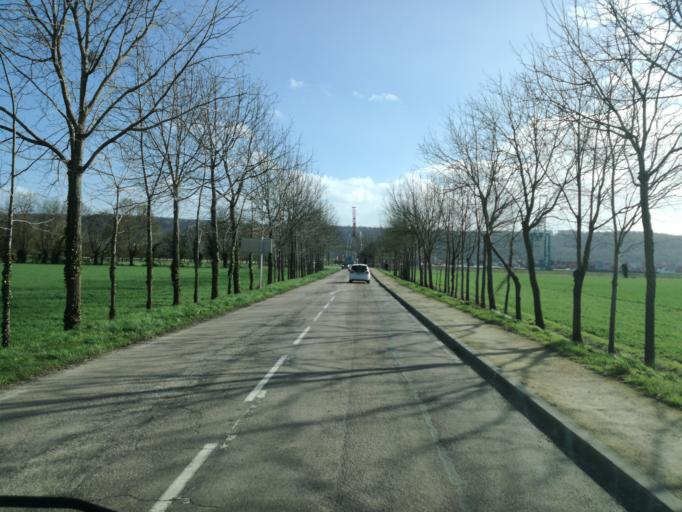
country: FR
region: Haute-Normandie
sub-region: Departement de la Seine-Maritime
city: Grand-Couronne
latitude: 49.3596
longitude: 0.9796
